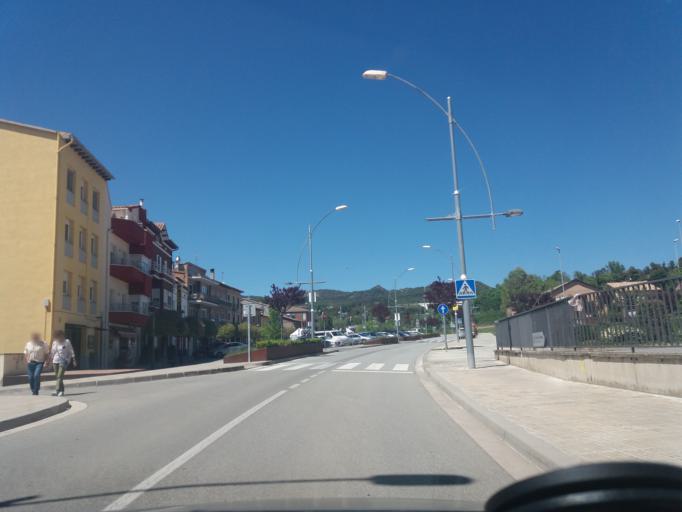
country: ES
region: Catalonia
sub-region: Provincia de Barcelona
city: Avia
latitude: 42.0699
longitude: 1.8699
